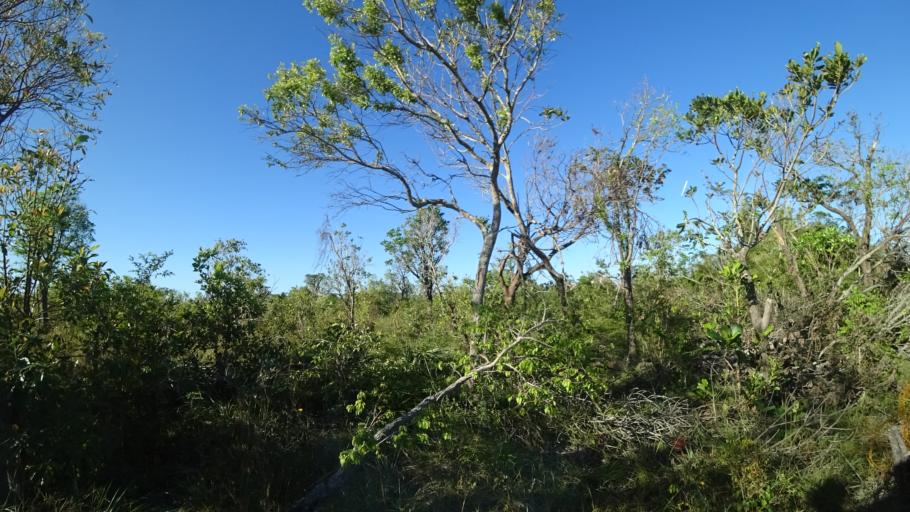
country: MZ
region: Sofala
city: Beira
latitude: -19.5709
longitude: 35.2478
